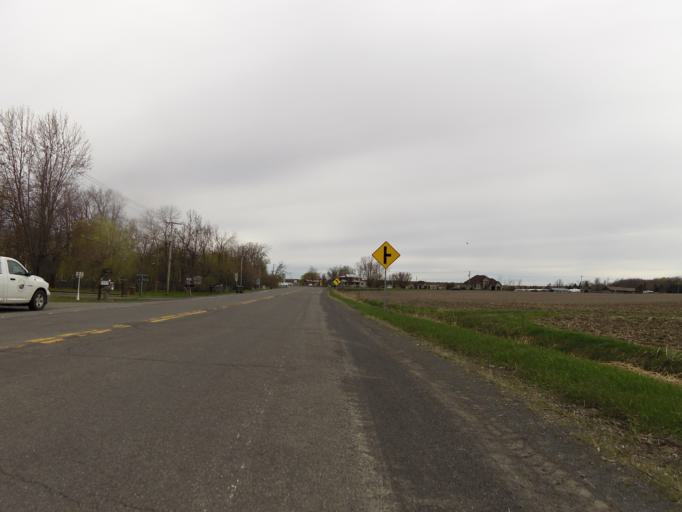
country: CA
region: Quebec
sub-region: Monteregie
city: Hudson
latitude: 45.5275
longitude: -74.1756
